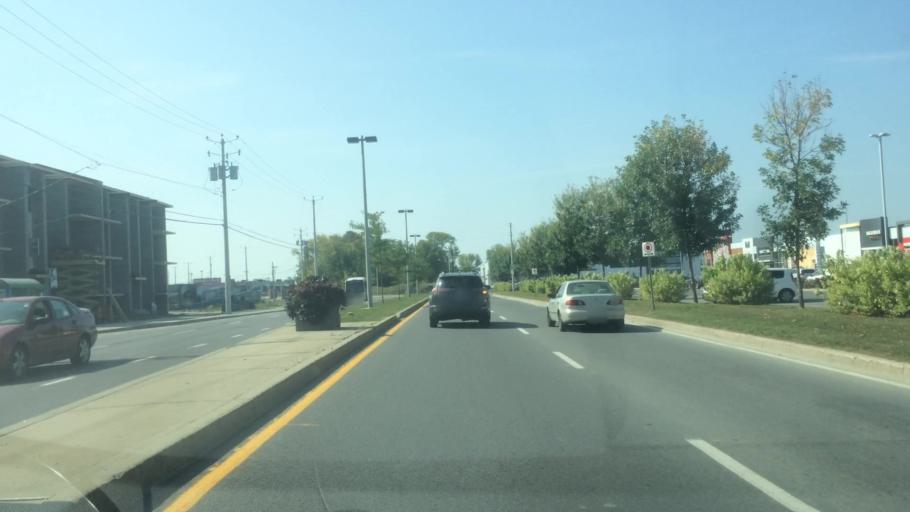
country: CA
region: Quebec
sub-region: Monteregie
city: Vaudreuil-Dorion
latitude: 45.4021
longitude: -74.0497
